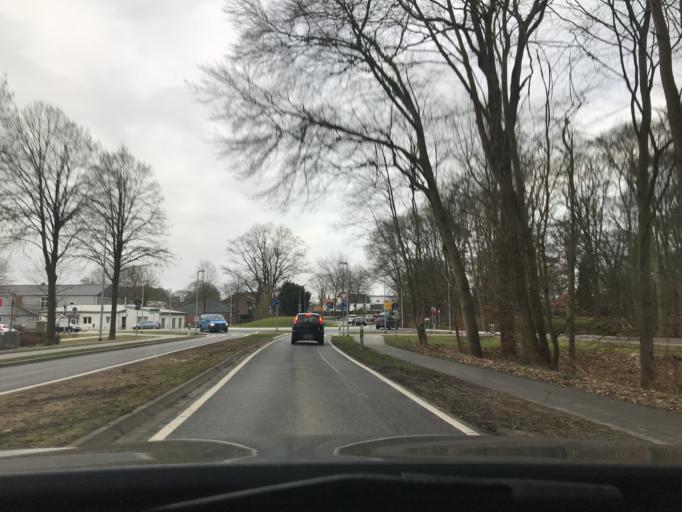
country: DE
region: North Rhine-Westphalia
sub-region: Regierungsbezirk Dusseldorf
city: Kleve
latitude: 51.7621
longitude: 6.1854
